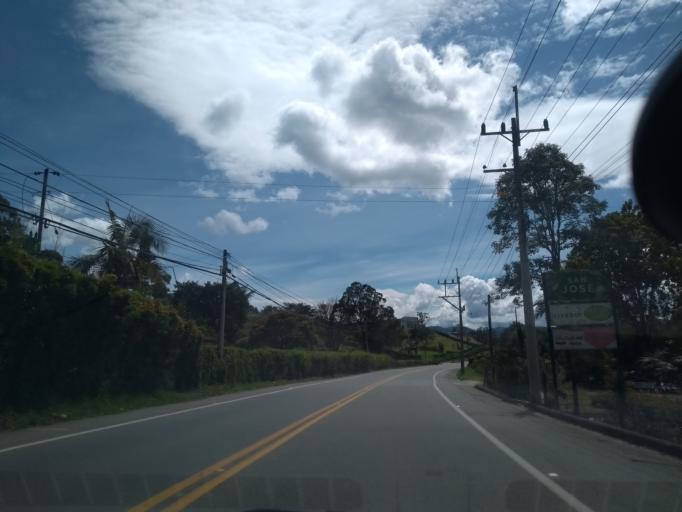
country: CO
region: Antioquia
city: Carmen de Viboral
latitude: 6.0998
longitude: -75.3833
